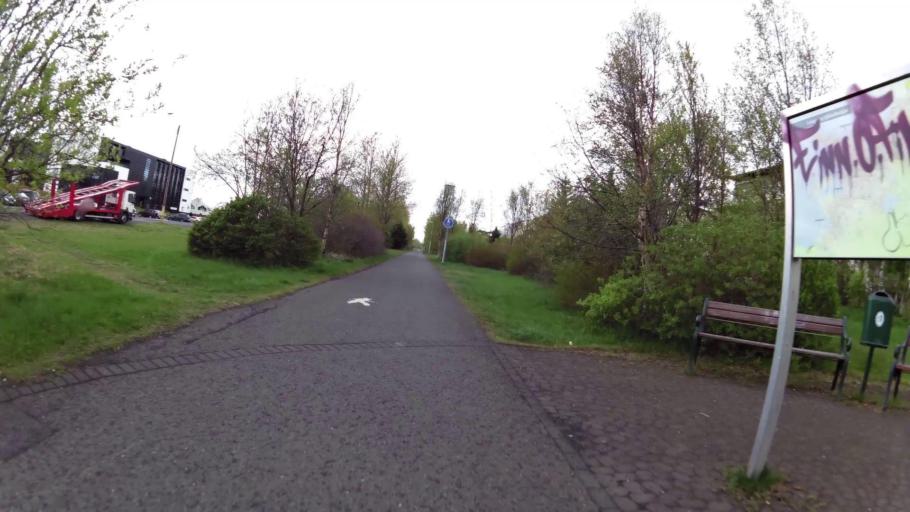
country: IS
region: Capital Region
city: Reykjavik
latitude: 64.1284
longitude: -21.8568
